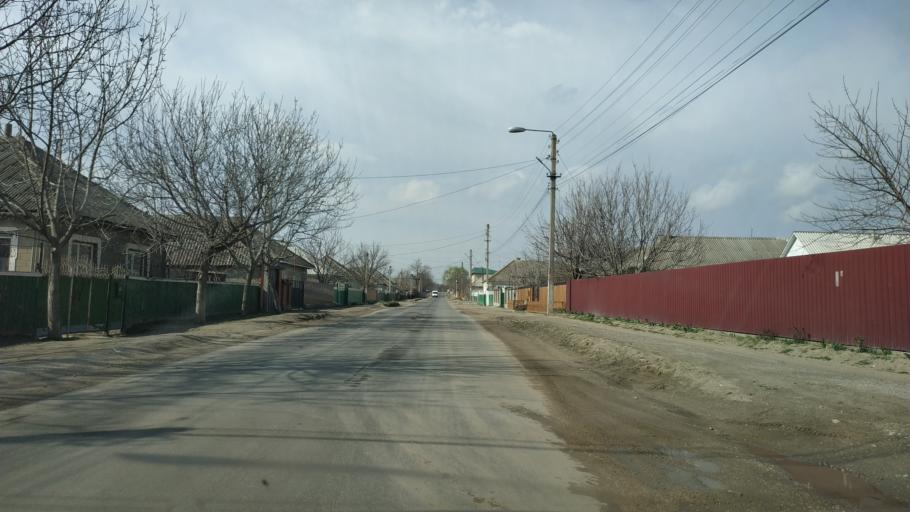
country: MD
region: Gagauzia
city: Vulcanesti
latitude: 45.6754
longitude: 28.4167
